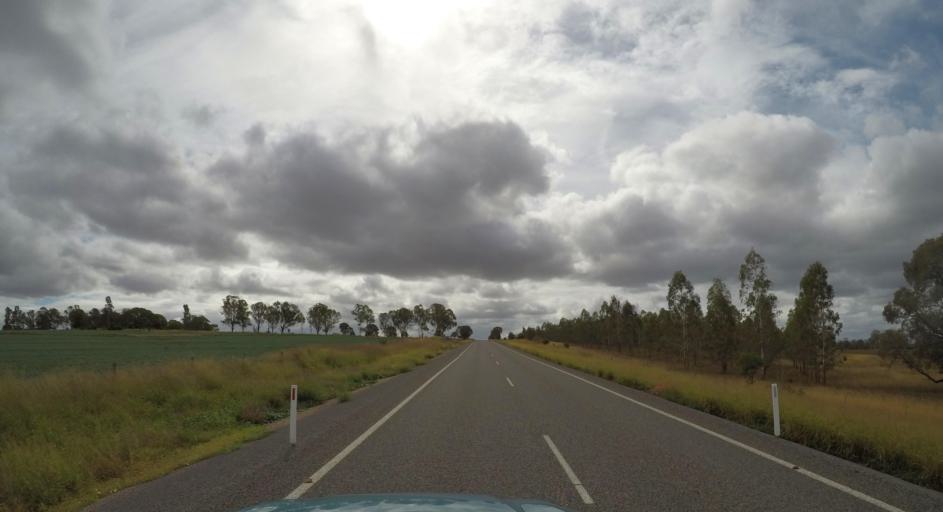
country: AU
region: Queensland
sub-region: South Burnett
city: Wondai
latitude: -26.3148
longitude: 151.2564
